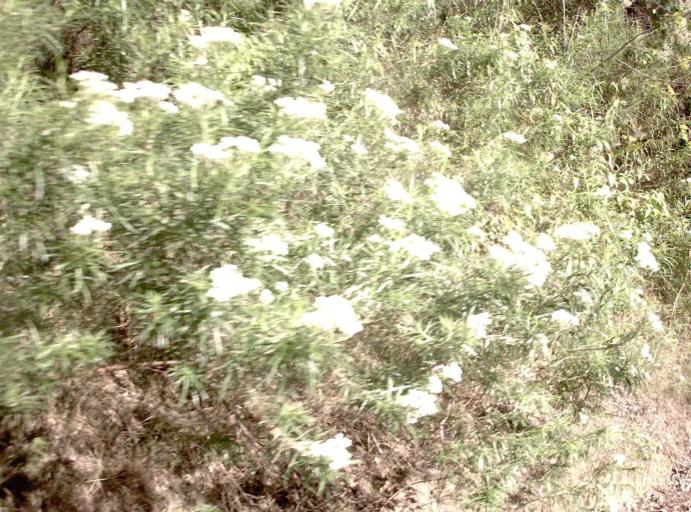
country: AU
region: Victoria
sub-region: East Gippsland
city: Lakes Entrance
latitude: -37.4847
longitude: 148.5538
